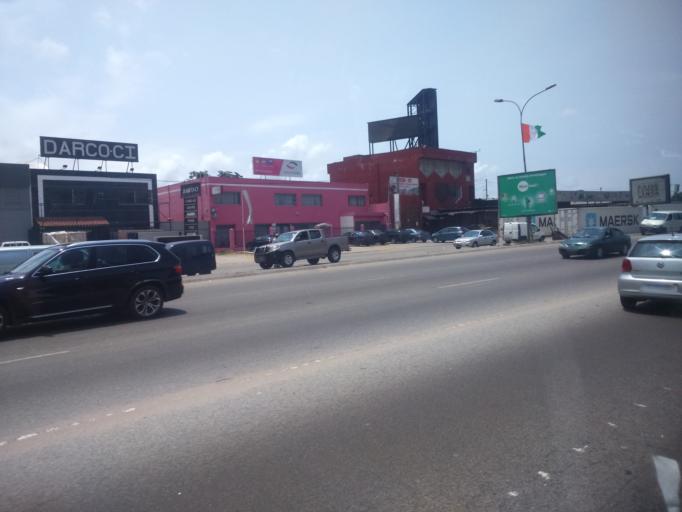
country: CI
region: Lagunes
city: Abidjan
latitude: 5.2907
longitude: -3.9720
